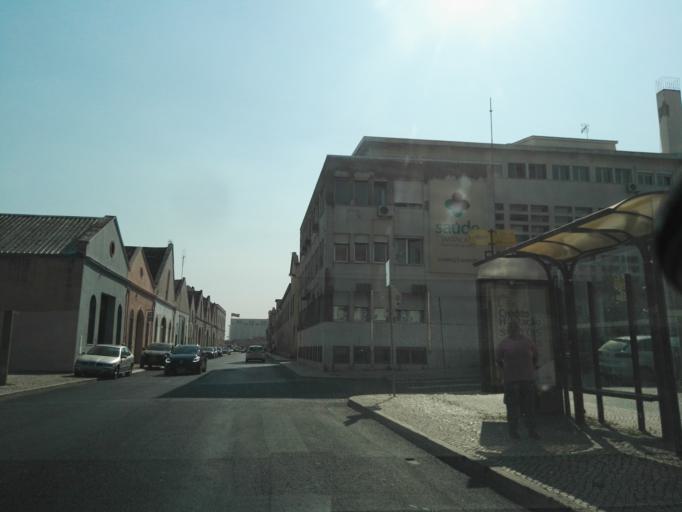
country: PT
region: Lisbon
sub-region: Lisbon
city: Lisbon
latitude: 38.7393
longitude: -9.1031
